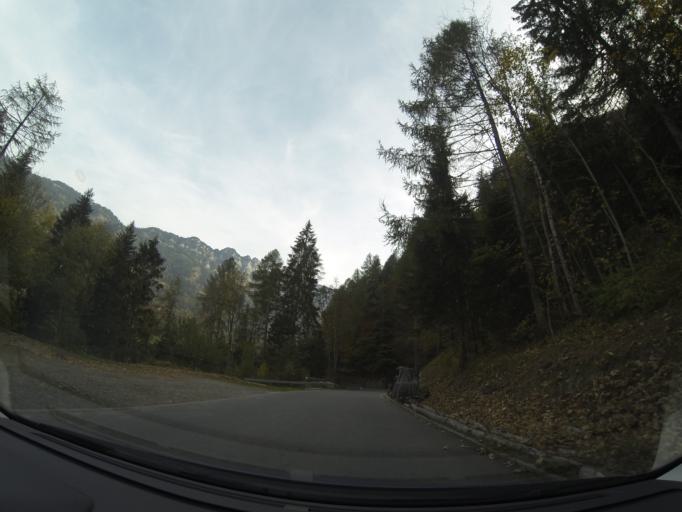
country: CH
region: Saint Gallen
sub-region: Wahlkreis Sarganserland
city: Bad Ragaz
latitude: 46.9596
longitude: 9.4728
